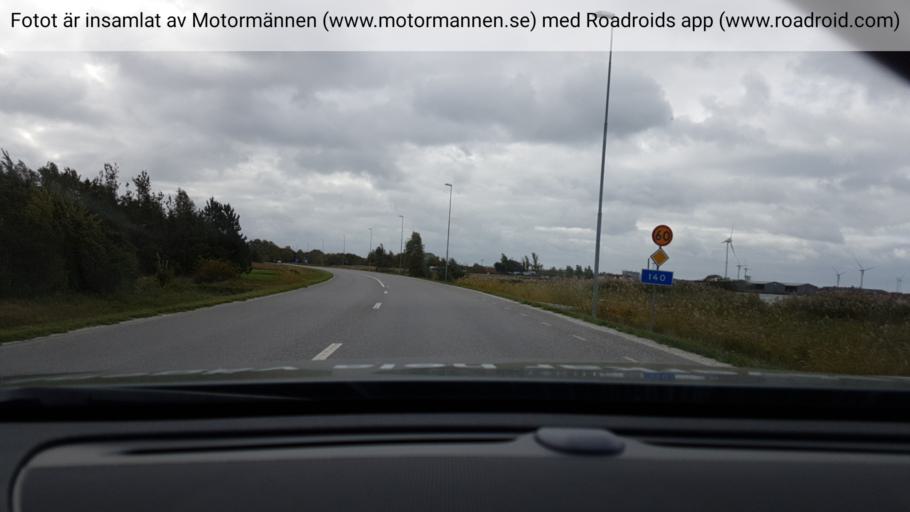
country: SE
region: Gotland
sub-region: Gotland
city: Klintehamn
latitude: 57.3934
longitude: 18.1955
